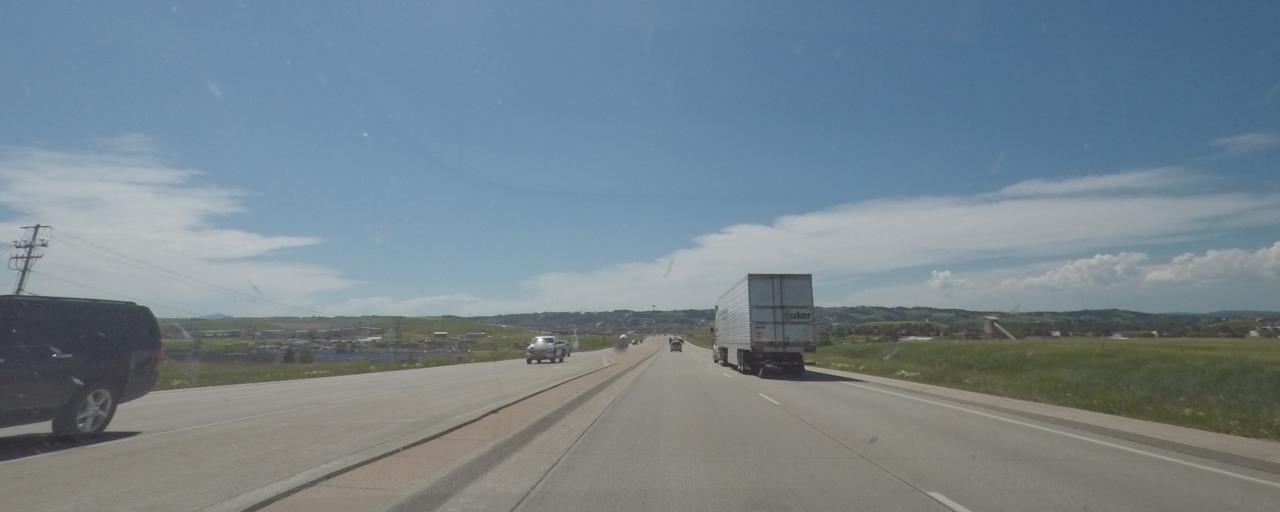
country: US
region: South Dakota
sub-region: Pennington County
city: Rapid Valley
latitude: 44.0390
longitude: -103.1810
